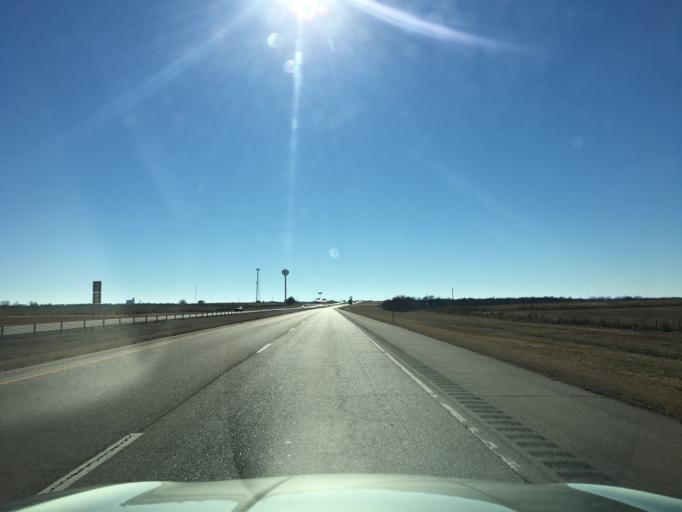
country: US
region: Oklahoma
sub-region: Kay County
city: Blackwell
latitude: 36.9507
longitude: -97.3458
